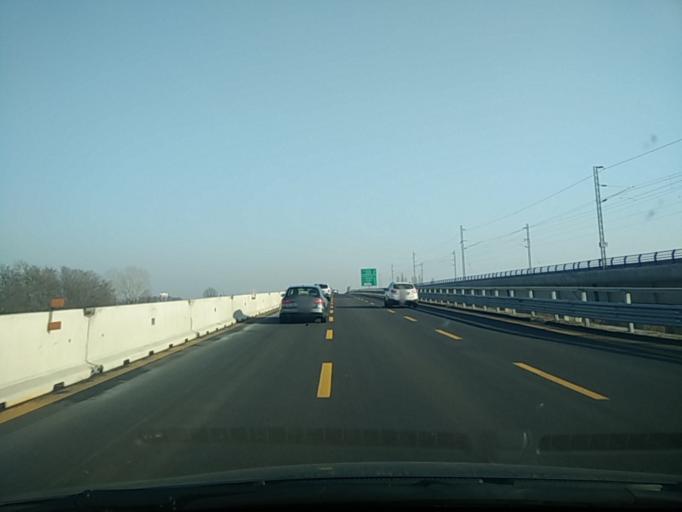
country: IT
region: Lombardy
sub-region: Citta metropolitana di Milano
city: Mantegazza
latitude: 45.5046
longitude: 8.9834
